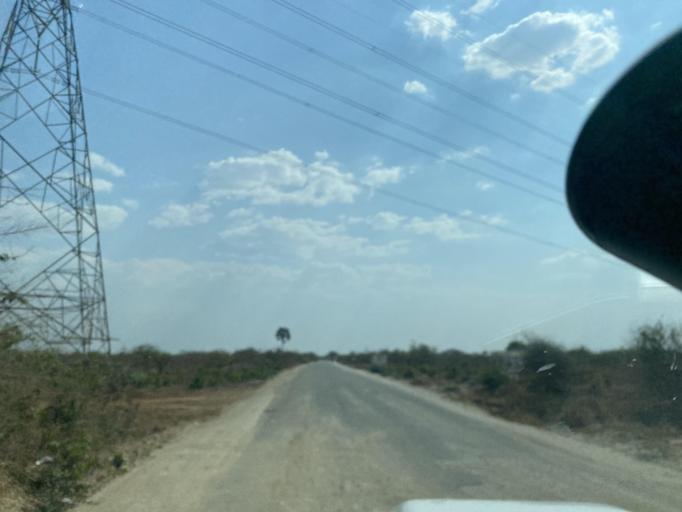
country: ZM
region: Lusaka
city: Lusaka
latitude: -15.3687
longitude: 28.0826
